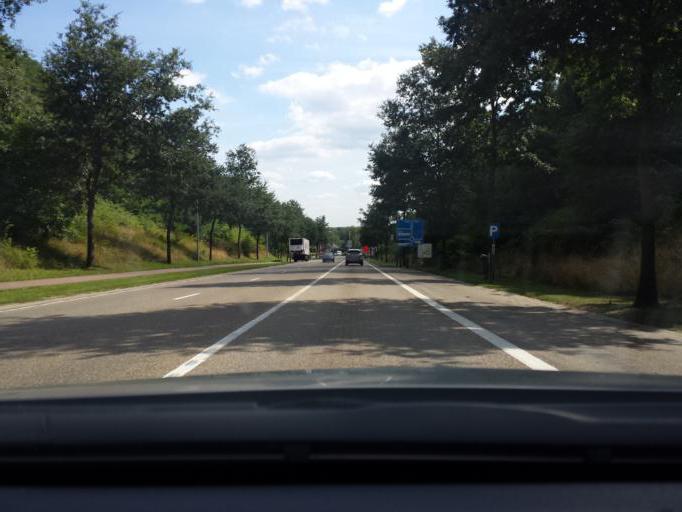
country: BE
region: Flanders
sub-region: Provincie Limburg
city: Lummen
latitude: 50.9910
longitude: 5.1977
